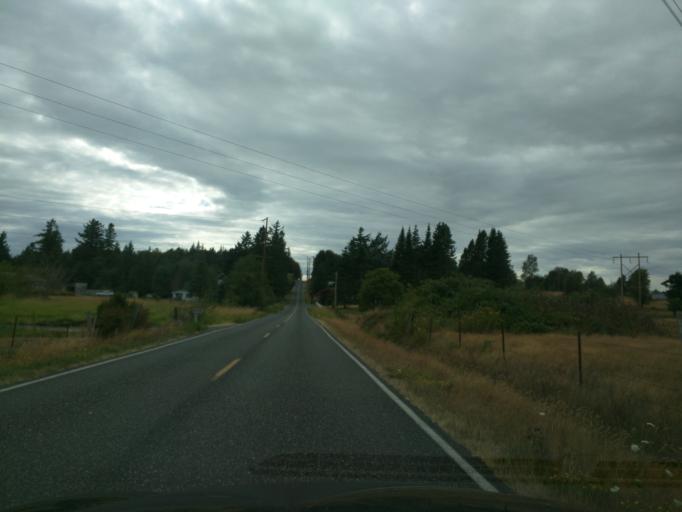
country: US
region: Washington
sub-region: Whatcom County
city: Bellingham
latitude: 48.8147
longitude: -122.4533
